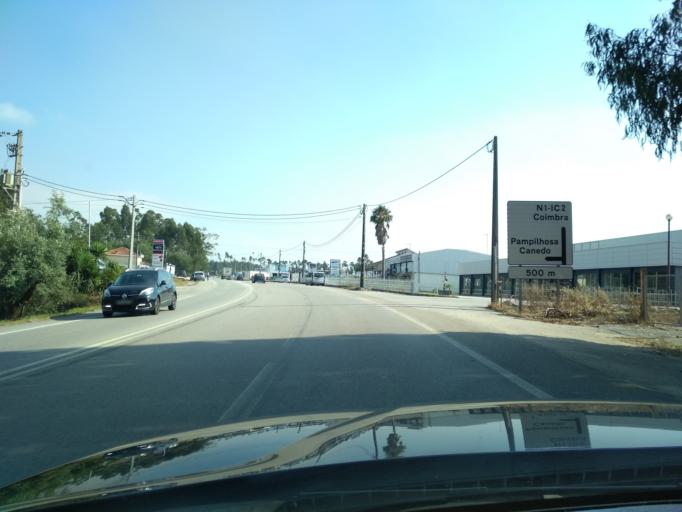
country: PT
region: Aveiro
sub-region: Mealhada
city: Pampilhosa do Botao
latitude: 40.3424
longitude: -8.4523
